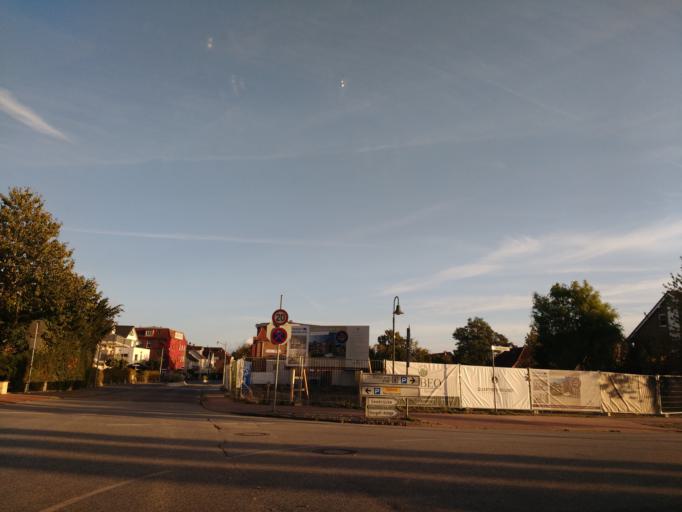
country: DE
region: Schleswig-Holstein
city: Kellenhusen
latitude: 54.1926
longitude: 11.0563
